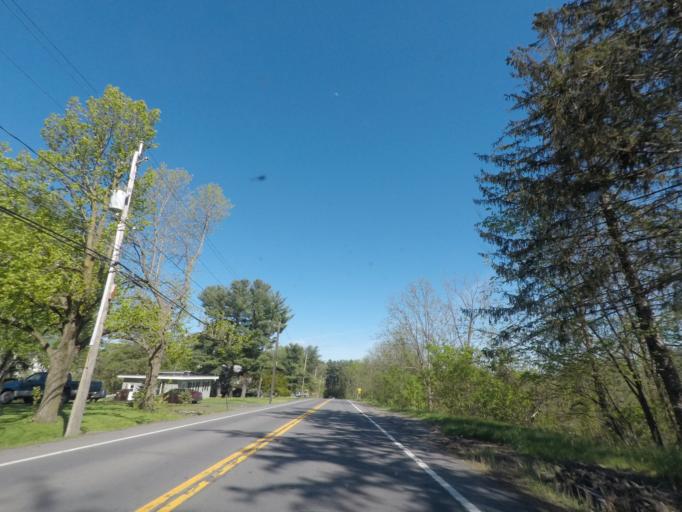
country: US
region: New York
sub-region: Albany County
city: Albany
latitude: 42.6198
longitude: -73.7722
